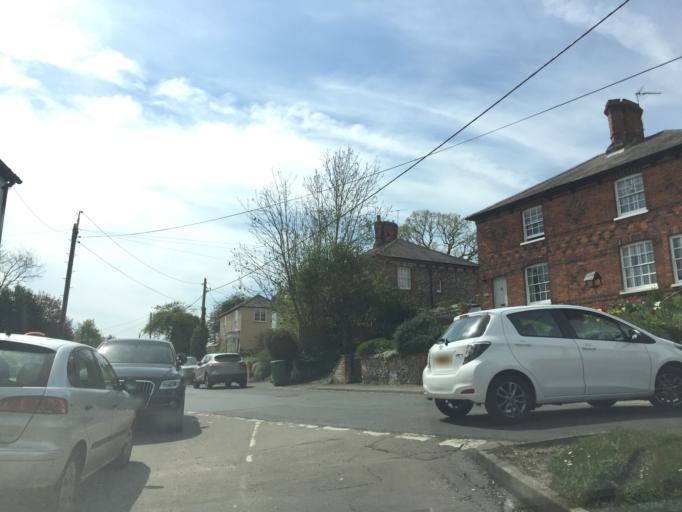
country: GB
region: England
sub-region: Essex
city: Elsenham
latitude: 51.9626
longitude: 0.2379
